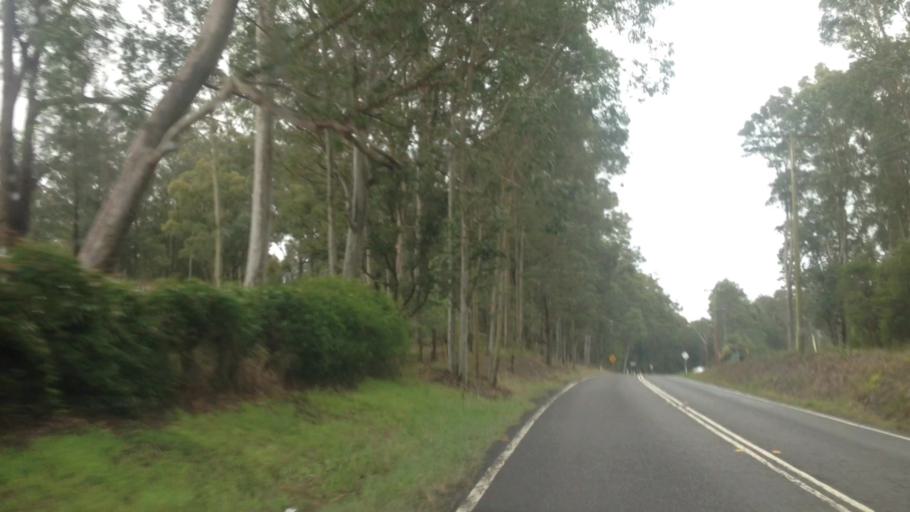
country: AU
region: New South Wales
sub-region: Wyong Shire
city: Little Jilliby
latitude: -33.2567
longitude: 151.3974
